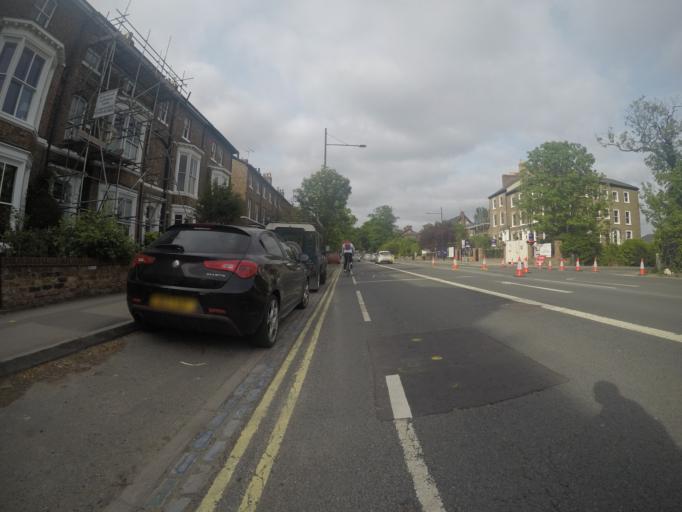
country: GB
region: England
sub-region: City of York
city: York
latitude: 53.9494
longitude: -1.0995
